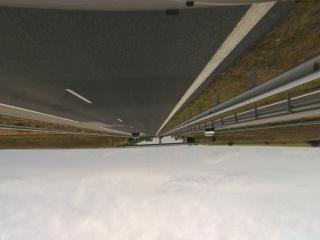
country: BG
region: Stara Zagora
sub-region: Obshtina Chirpan
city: Chirpan
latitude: 42.2000
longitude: 25.2780
